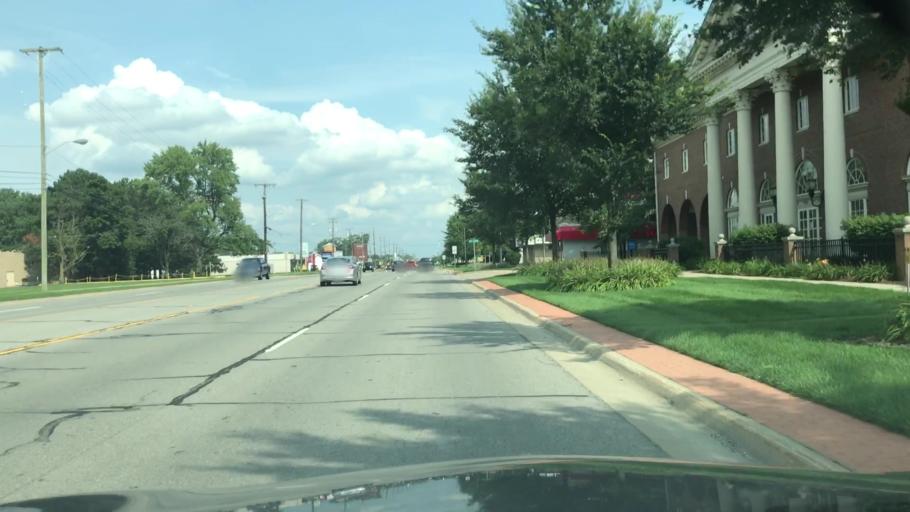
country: US
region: Michigan
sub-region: Wayne County
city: Plymouth
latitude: 42.3585
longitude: -83.4766
